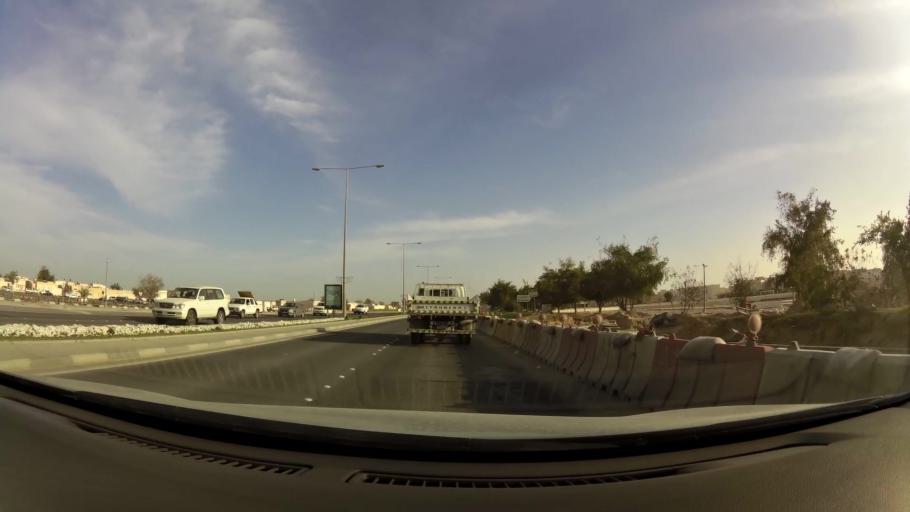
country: QA
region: Al Wakrah
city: Al Wakrah
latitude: 25.1728
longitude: 51.6067
